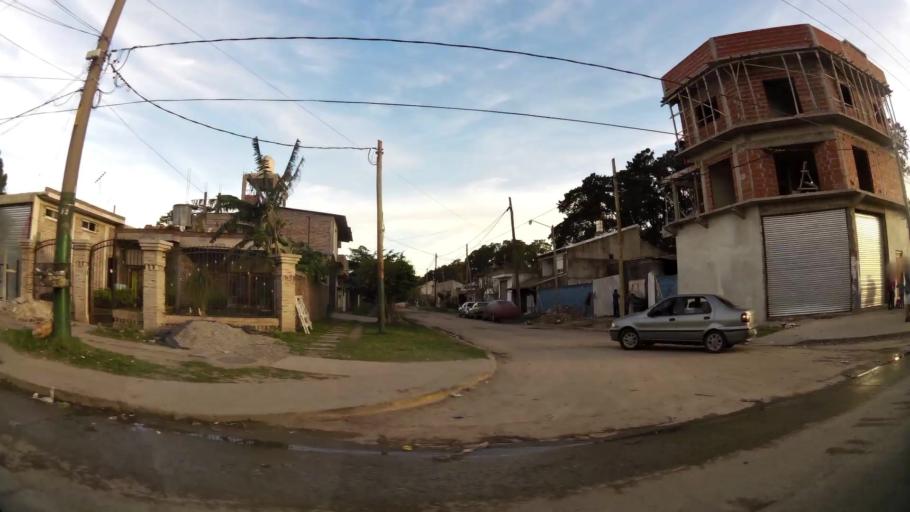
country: AR
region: Buenos Aires
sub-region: Partido de Almirante Brown
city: Adrogue
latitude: -34.7767
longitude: -58.3300
